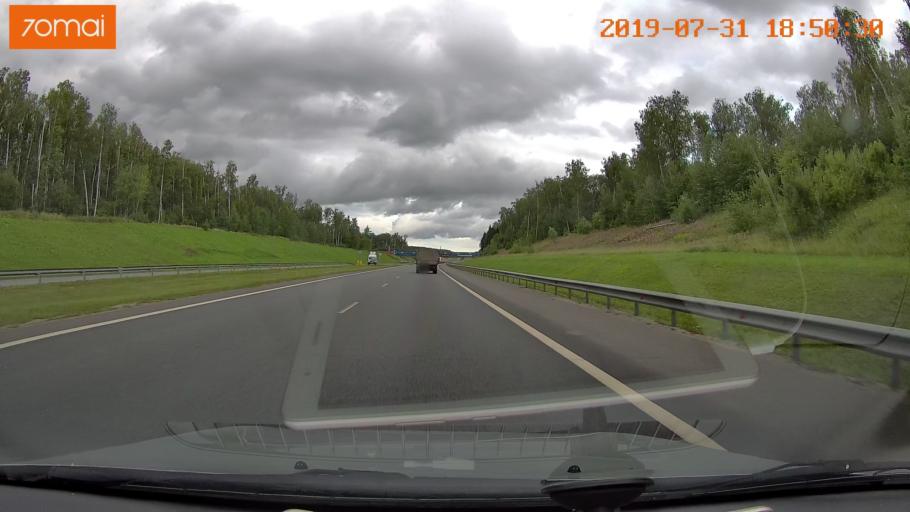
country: RU
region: Moskovskaya
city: Troitskoye
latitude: 55.2284
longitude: 38.5835
